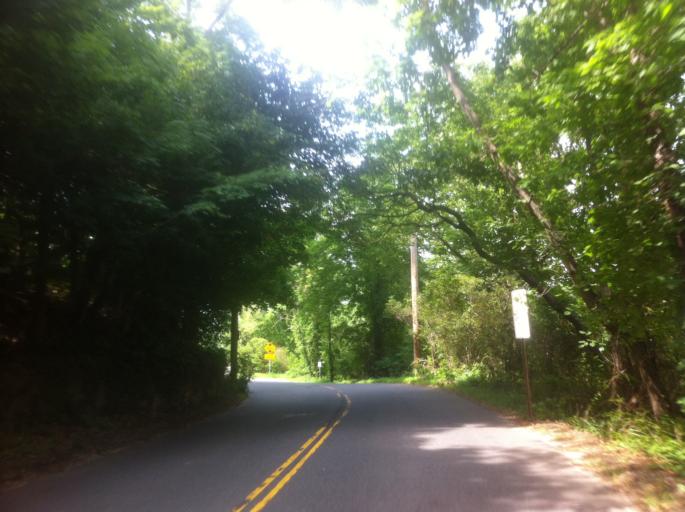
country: US
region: New York
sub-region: Nassau County
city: Oyster Bay
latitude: 40.8702
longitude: -73.5421
